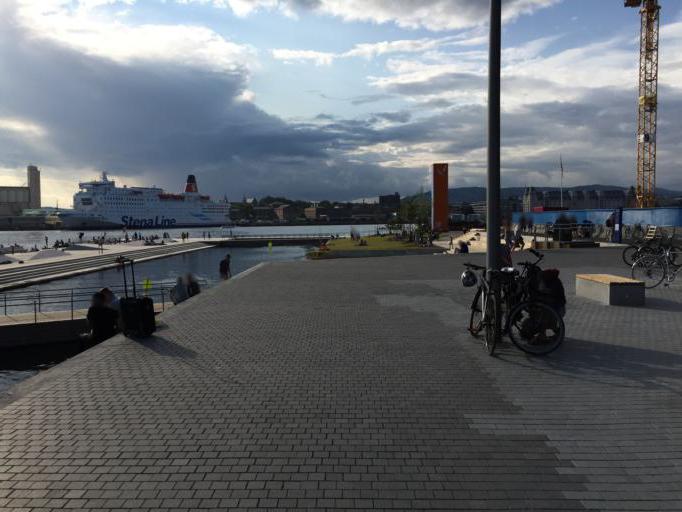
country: NO
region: Oslo
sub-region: Oslo
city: Oslo
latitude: 59.9008
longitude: 10.7518
